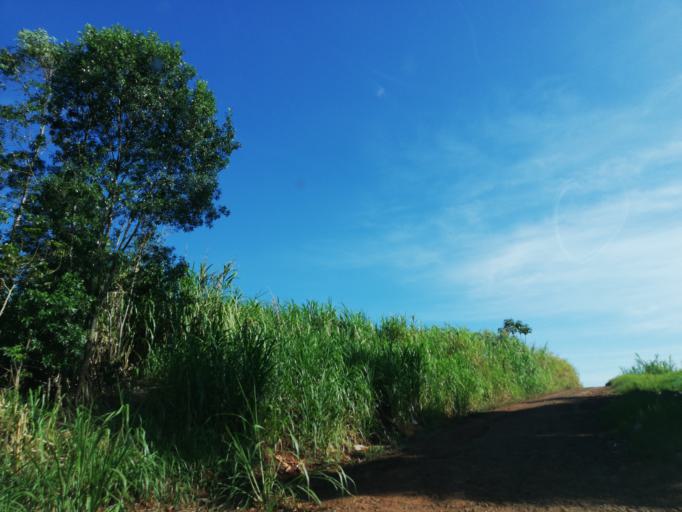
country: AR
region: Misiones
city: Dos de Mayo
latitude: -26.9899
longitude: -54.4952
